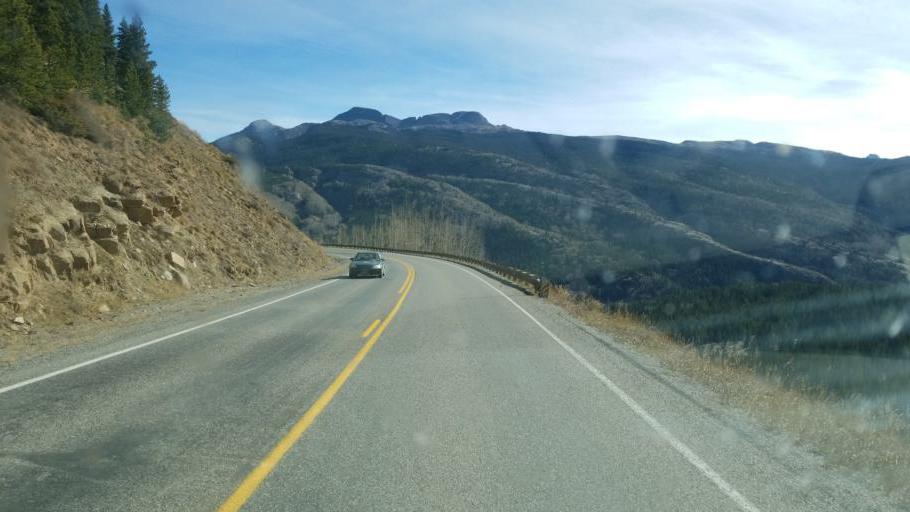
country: US
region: Colorado
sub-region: San Juan County
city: Silverton
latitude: 37.7082
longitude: -107.7674
